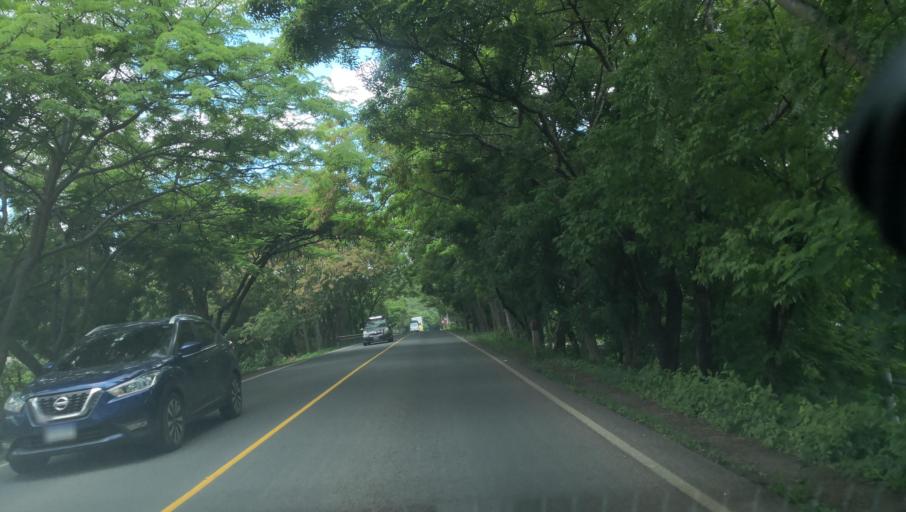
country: NI
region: Madriz
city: Yalaguina
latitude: 13.4799
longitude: -86.4875
